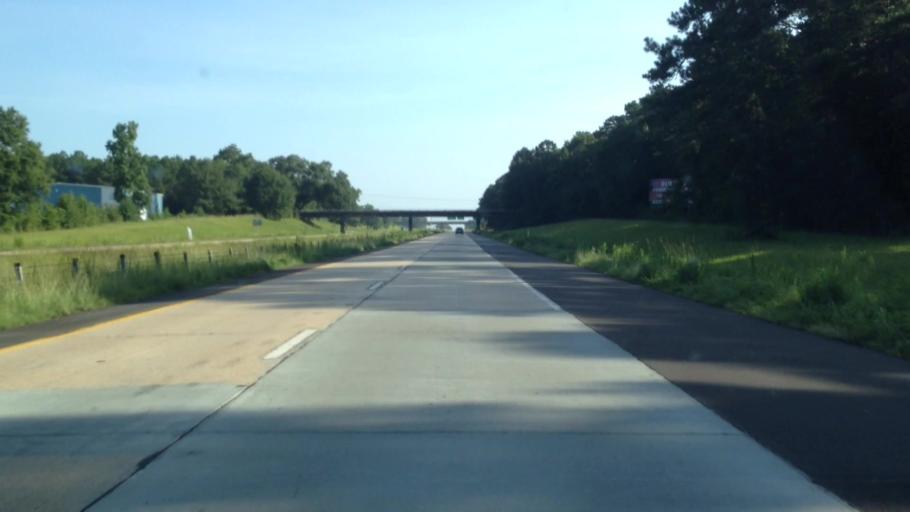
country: US
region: Mississippi
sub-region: Pike County
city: Summit
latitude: 31.2815
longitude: -90.4787
